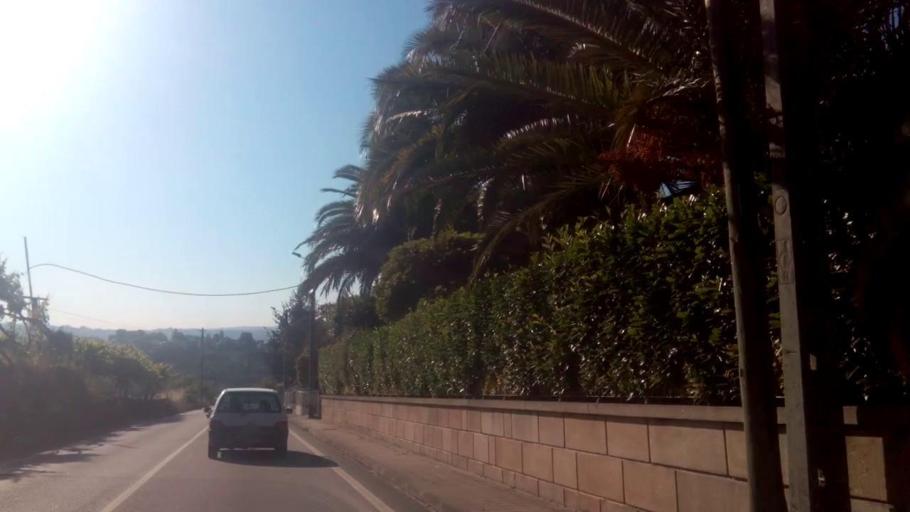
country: PT
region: Porto
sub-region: Penafiel
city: Penafiel
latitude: 41.1956
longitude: -8.2729
